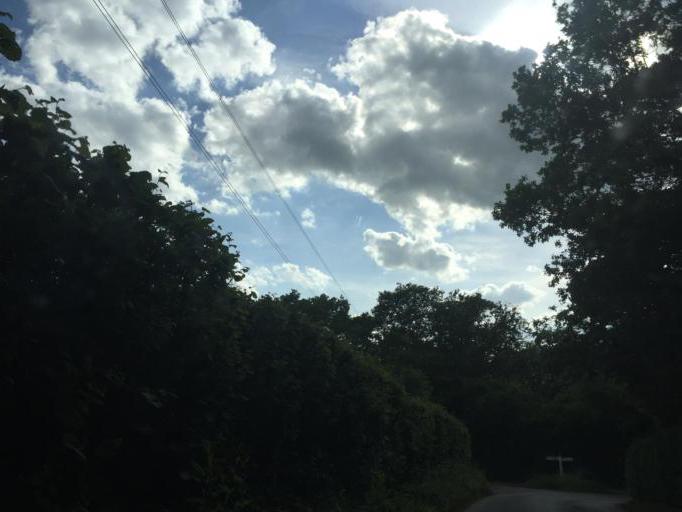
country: GB
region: England
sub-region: East Sussex
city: Wadhurst
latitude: 51.0338
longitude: 0.2833
